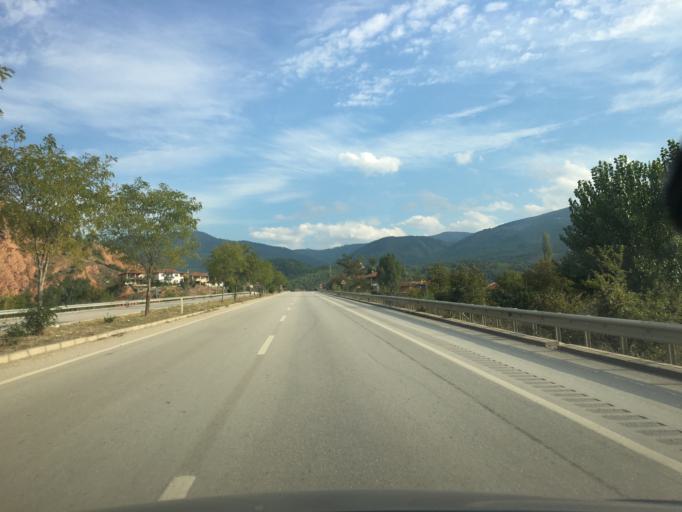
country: TR
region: Karabuk
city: Karabuk
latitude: 41.0984
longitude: 32.6733
